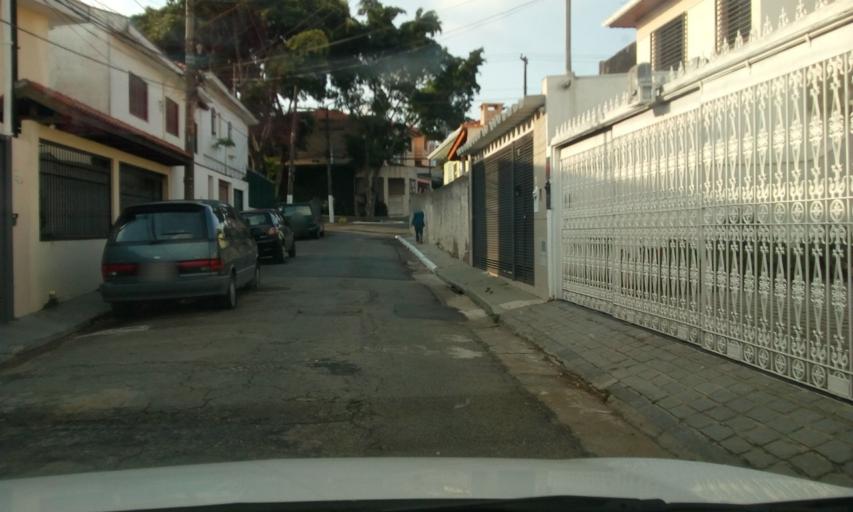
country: BR
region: Sao Paulo
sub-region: Diadema
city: Diadema
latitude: -23.6206
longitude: -46.6515
